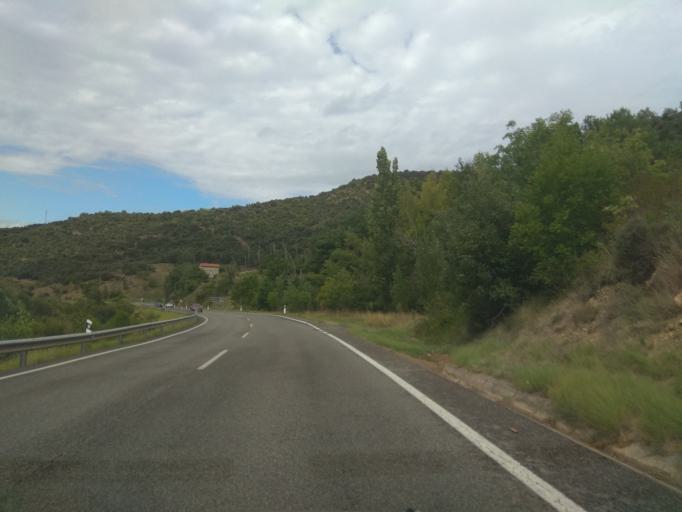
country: ES
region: Catalonia
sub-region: Provincia de Lleida
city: Alas i Cerc
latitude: 42.3592
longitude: 1.5181
